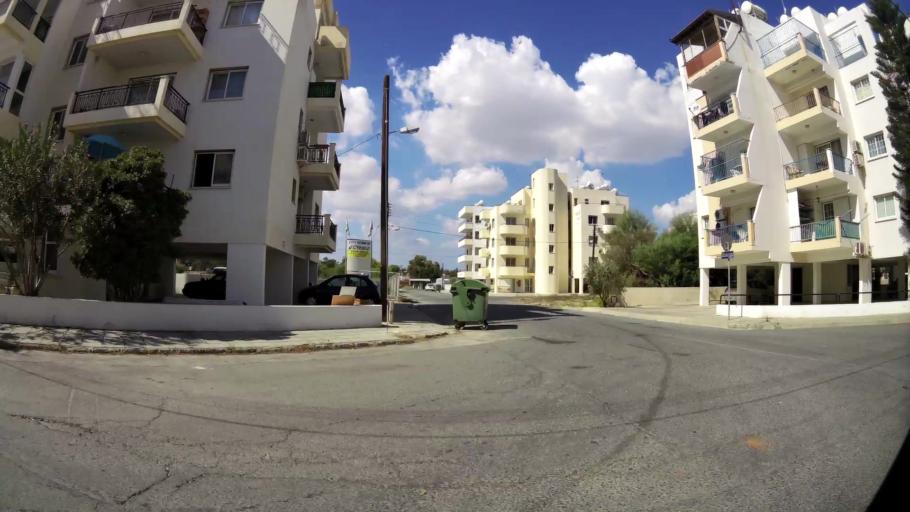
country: CY
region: Larnaka
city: Larnaca
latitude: 34.9036
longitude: 33.6350
